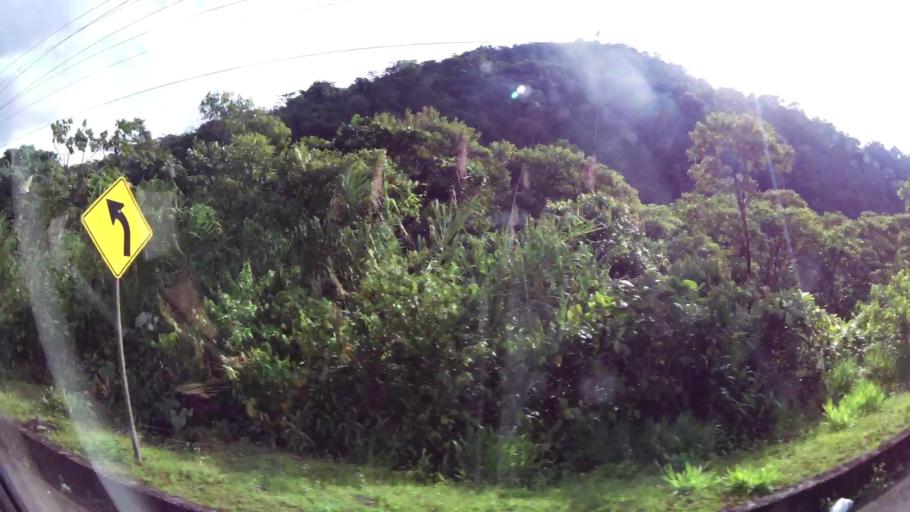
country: EC
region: Pastaza
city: Puyo
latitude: -1.4142
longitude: -78.1824
